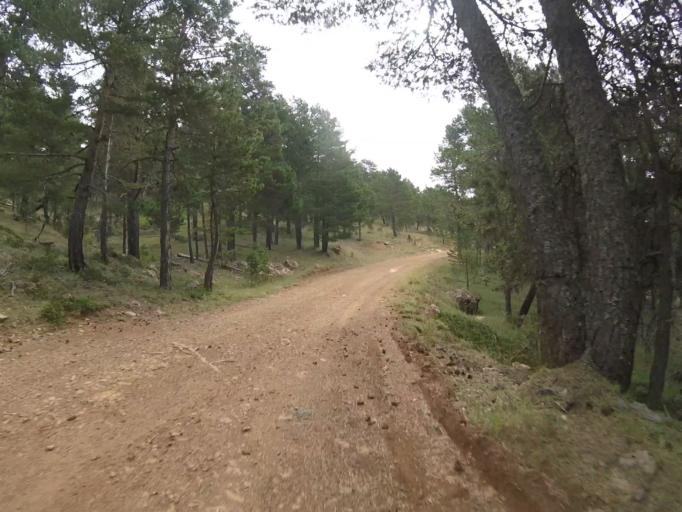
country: ES
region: Aragon
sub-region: Provincia de Teruel
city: Valdelinares
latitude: 40.3614
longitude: -0.6106
